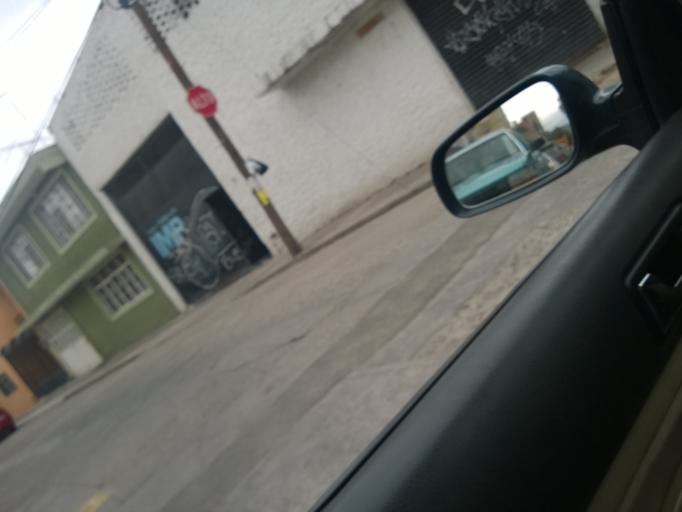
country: MX
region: Guanajuato
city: Leon
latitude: 21.1442
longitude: -101.6727
